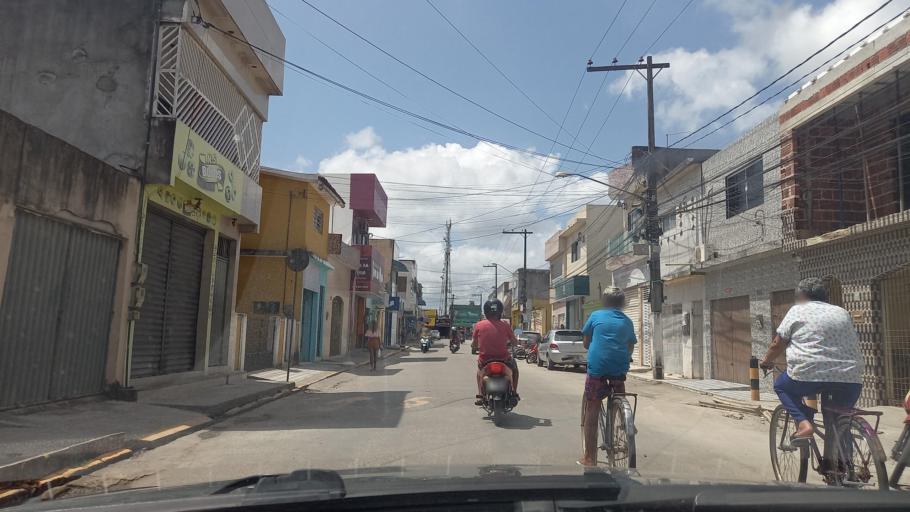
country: BR
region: Pernambuco
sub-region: Goiana
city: Goiana
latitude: -7.5599
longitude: -35.0026
